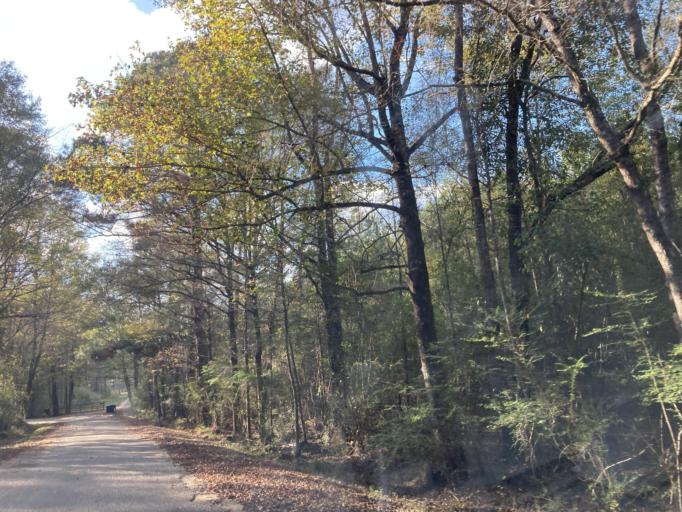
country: US
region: Mississippi
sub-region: Lamar County
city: Sumrall
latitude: 31.4465
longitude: -89.5879
